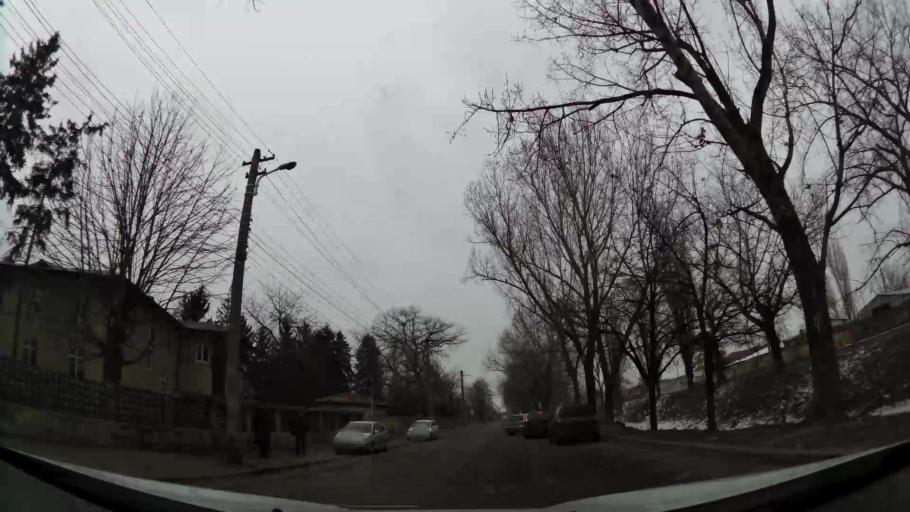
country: RO
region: Prahova
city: Ploiesti
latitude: 44.9455
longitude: 26.0386
